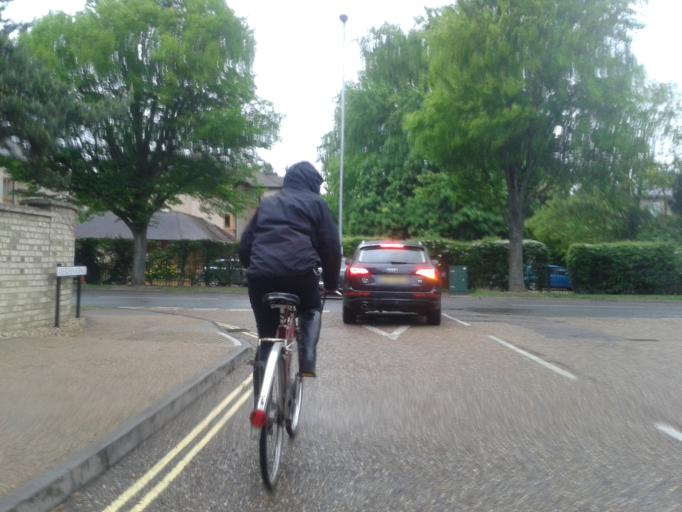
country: GB
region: England
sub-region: Cambridgeshire
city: Cambridge
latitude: 52.1916
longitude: 0.1284
